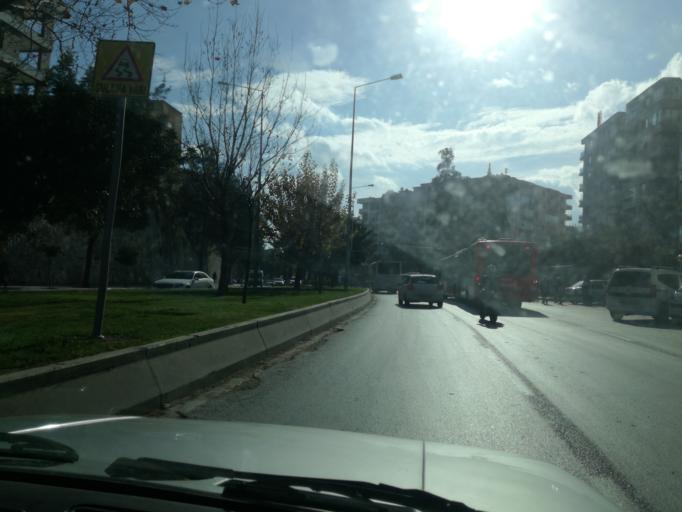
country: TR
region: Izmir
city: Izmir
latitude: 38.4056
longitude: 27.1223
